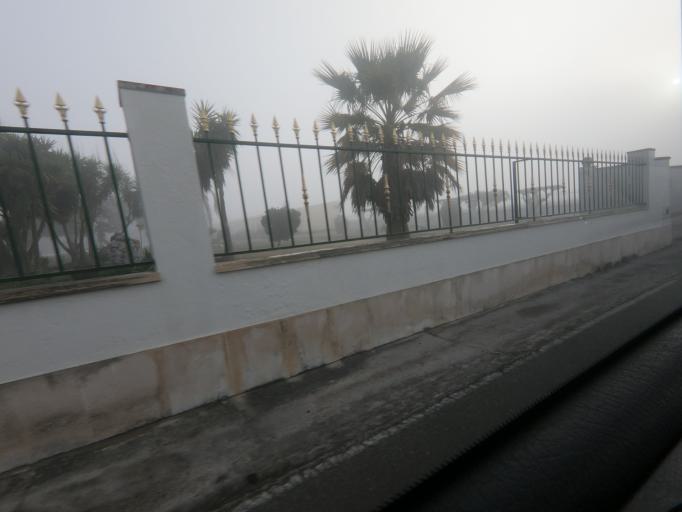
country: PT
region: Setubal
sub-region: Palmela
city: Palmela
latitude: 38.6047
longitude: -8.8501
